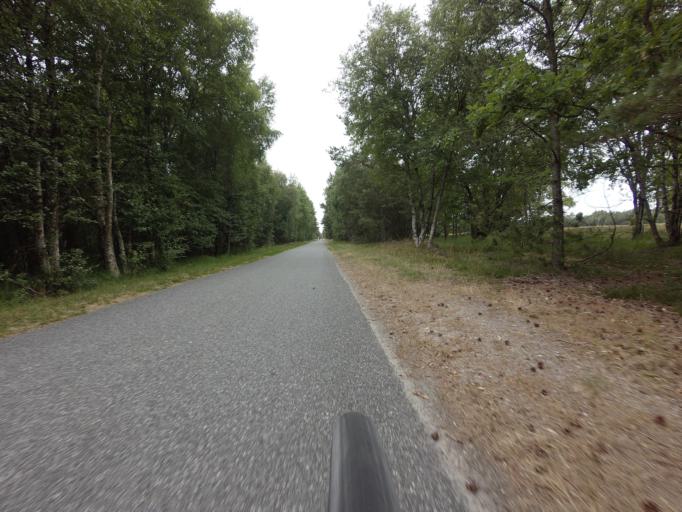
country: DK
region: North Denmark
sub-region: Laeso Kommune
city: Byrum
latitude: 57.2758
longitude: 10.9648
